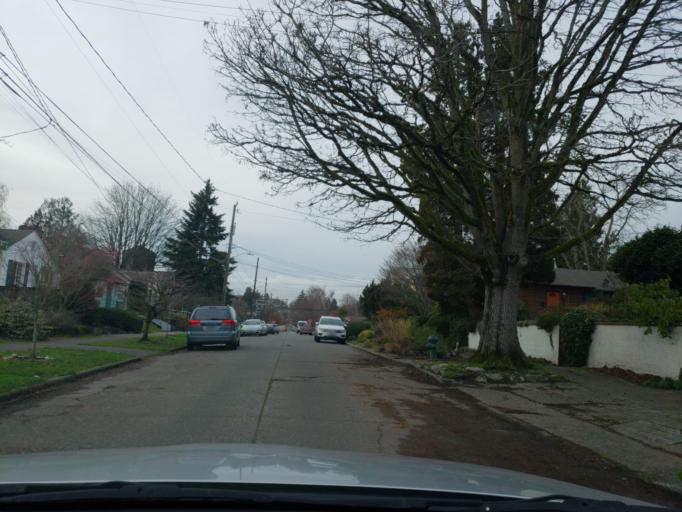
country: US
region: Washington
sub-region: King County
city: Shoreline
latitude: 47.6877
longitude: -122.3482
